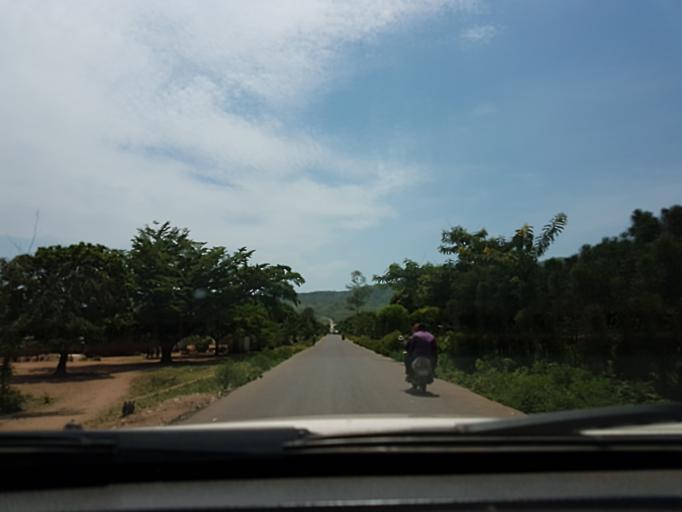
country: BI
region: Cibitoke
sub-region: Commune of Buganda
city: Buganda
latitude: -3.0813
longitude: 29.1250
